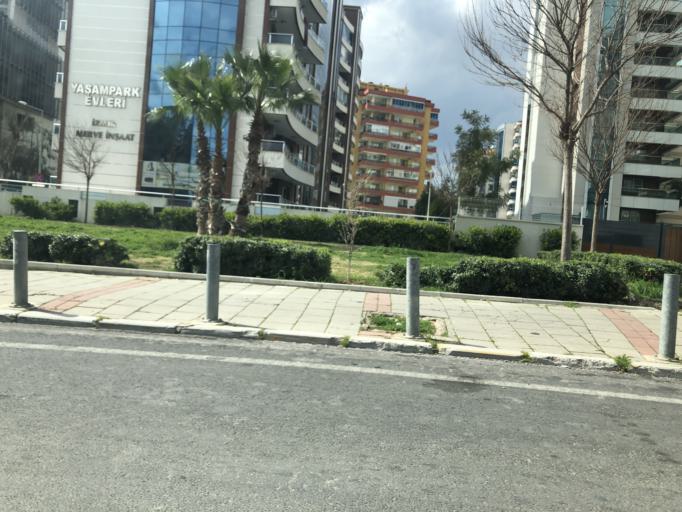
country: TR
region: Izmir
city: Karabaglar
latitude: 38.3899
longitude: 27.0448
